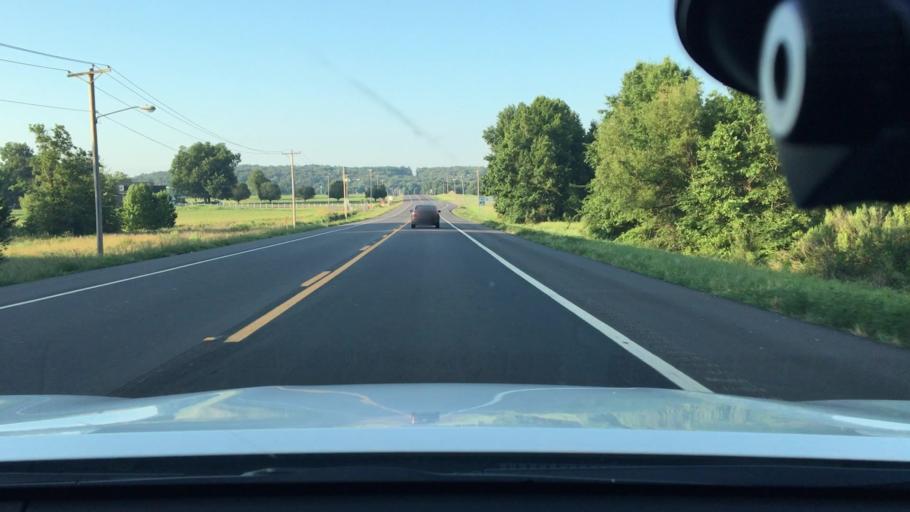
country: US
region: Arkansas
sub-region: Johnson County
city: Clarksville
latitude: 35.4352
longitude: -93.5294
